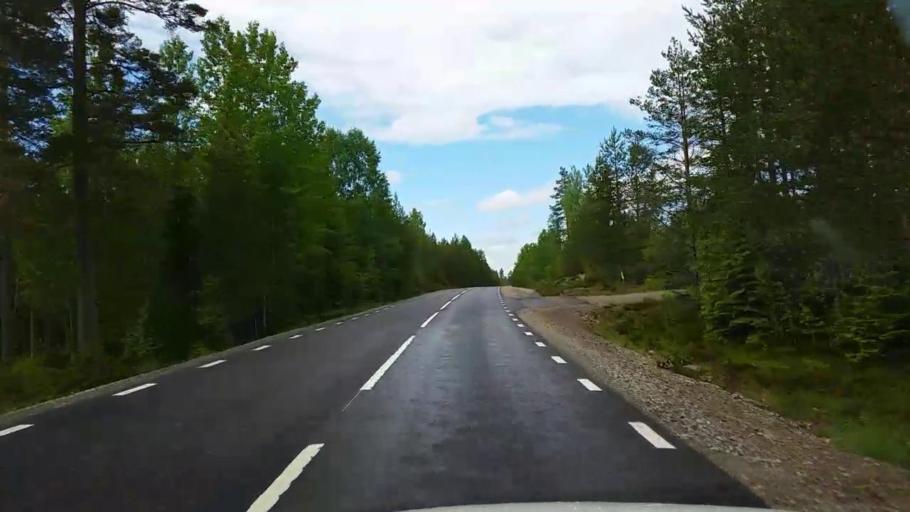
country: SE
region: Gaevleborg
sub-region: Sandvikens Kommun
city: Jarbo
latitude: 60.8704
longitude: 16.4090
